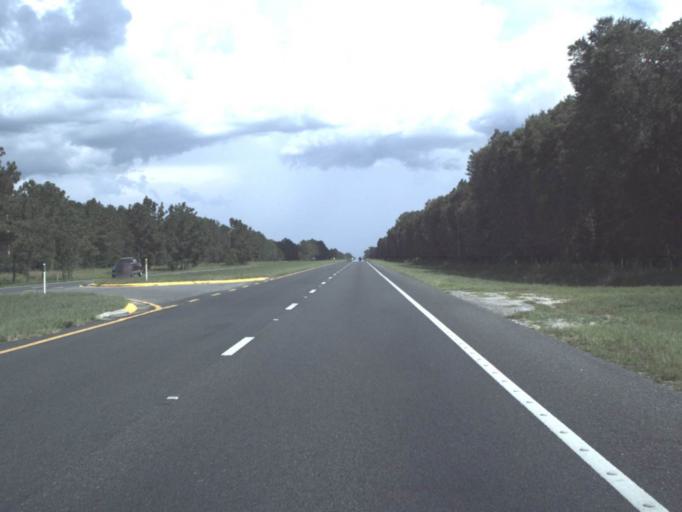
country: US
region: Florida
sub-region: Levy County
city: Chiefland
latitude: 29.4326
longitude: -82.8331
